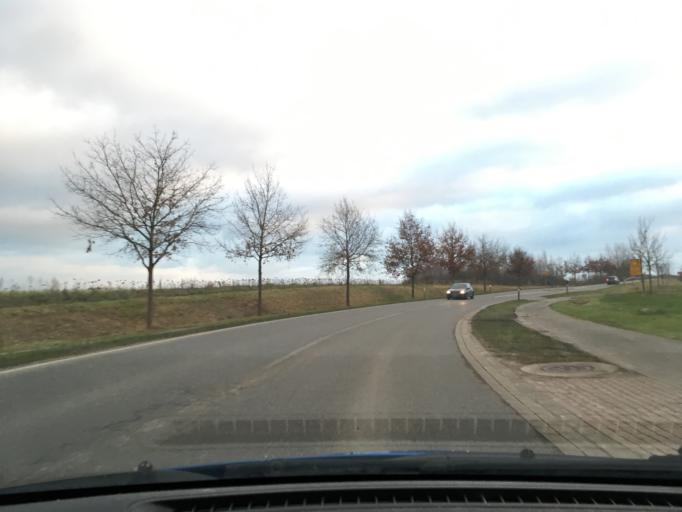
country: DE
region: Lower Saxony
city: Wrestedt
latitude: 52.9192
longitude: 10.5278
